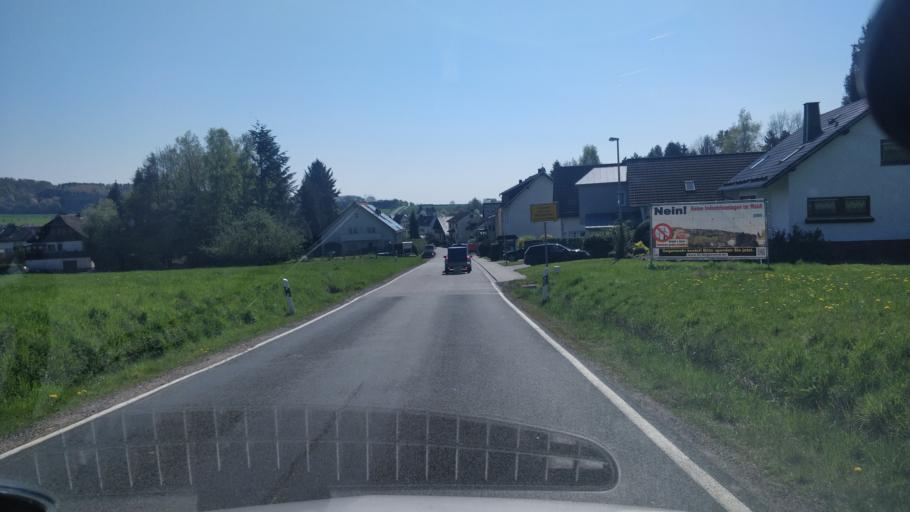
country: DE
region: Hesse
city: Waldbrunn
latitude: 50.5260
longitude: 8.0891
